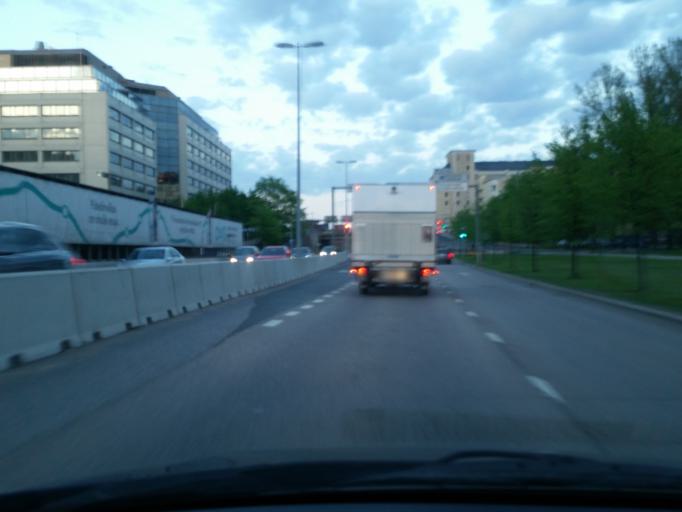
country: FI
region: Uusimaa
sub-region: Helsinki
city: Helsinki
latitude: 60.1901
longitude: 24.9593
